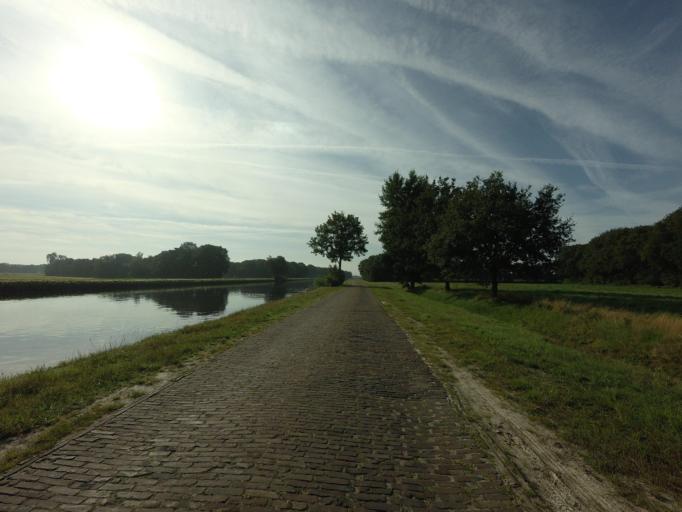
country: NL
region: Drenthe
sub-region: Gemeente Tynaarlo
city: Tynaarlo
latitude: 53.0544
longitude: 6.6061
